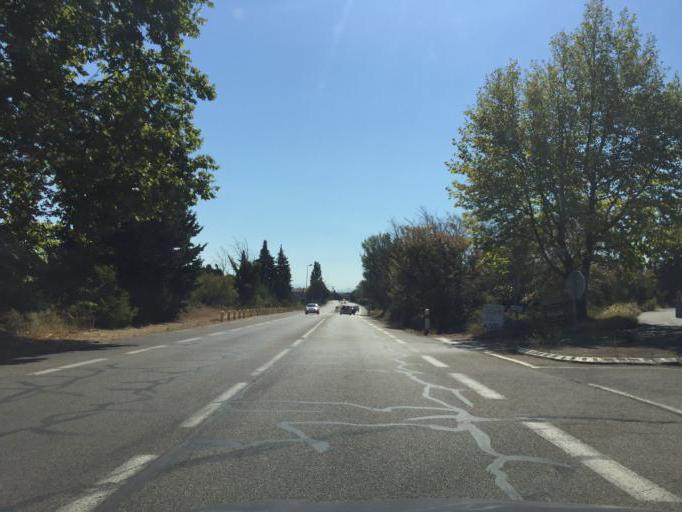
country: FR
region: Provence-Alpes-Cote d'Azur
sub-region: Departement du Vaucluse
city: Saint-Saturnin-les-Avignon
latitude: 43.9678
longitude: 4.9214
